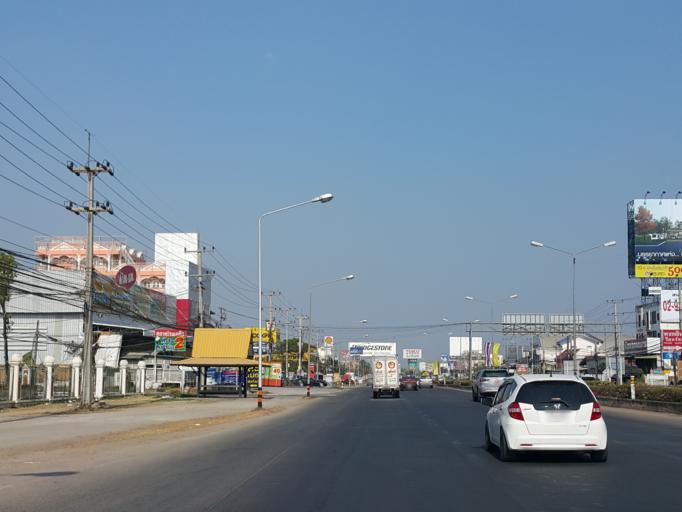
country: TH
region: Phitsanulok
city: Phitsanulok
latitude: 16.8183
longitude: 100.2897
